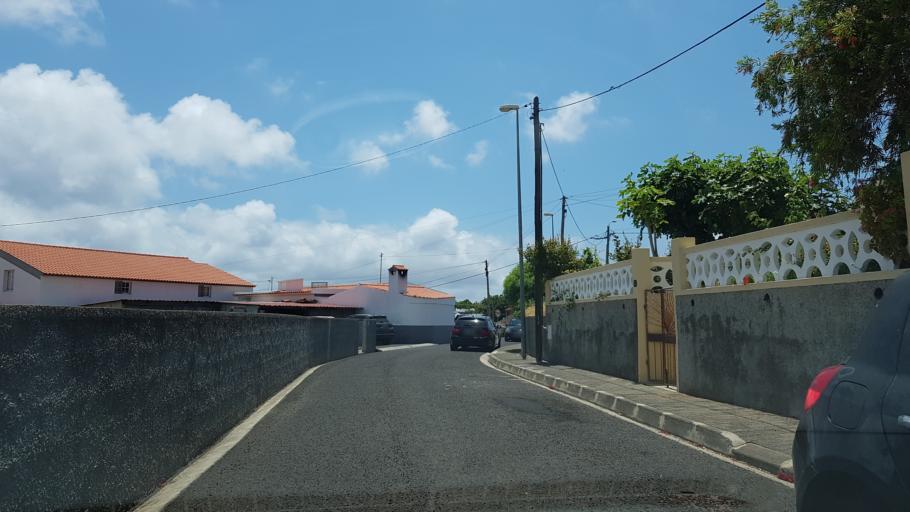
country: PT
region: Madeira
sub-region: Porto Santo
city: Vila de Porto Santo
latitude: 33.0696
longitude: -16.3387
